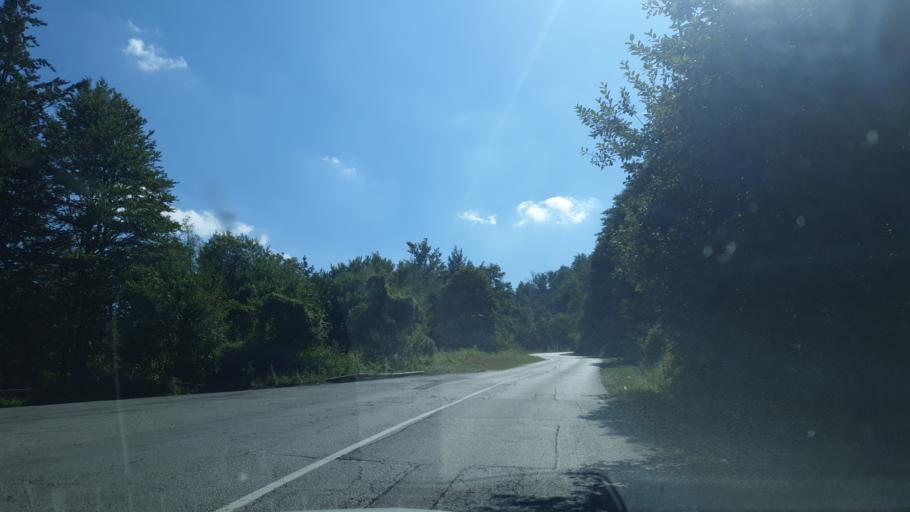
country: RS
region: Central Serbia
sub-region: Kolubarski Okrug
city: Mionica
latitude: 44.1359
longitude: 20.0186
